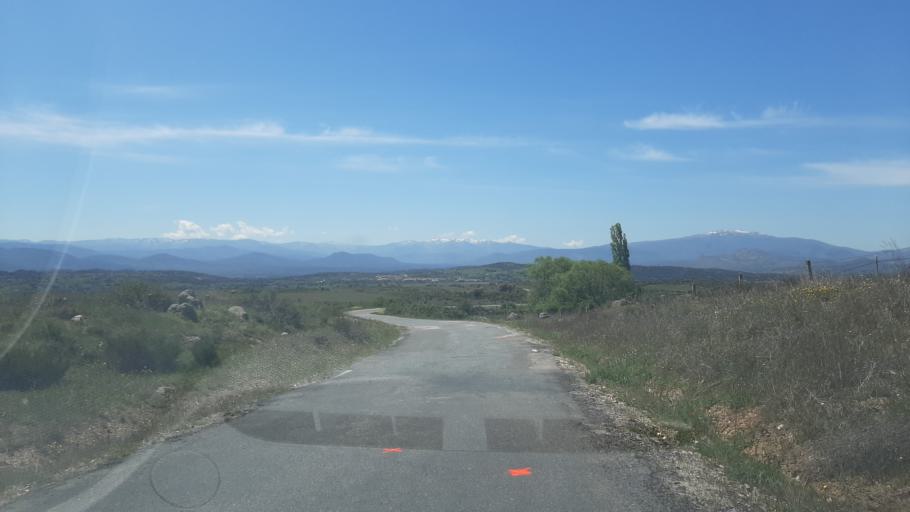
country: ES
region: Castille and Leon
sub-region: Provincia de Avila
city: Narrillos del Alamo
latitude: 40.5642
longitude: -5.4366
